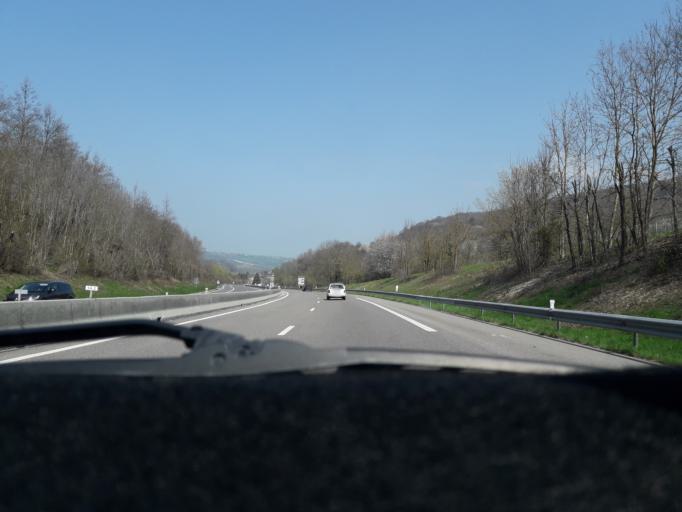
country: FR
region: Rhone-Alpes
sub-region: Departement de l'Isere
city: Chabons
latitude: 45.4606
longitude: 5.4021
